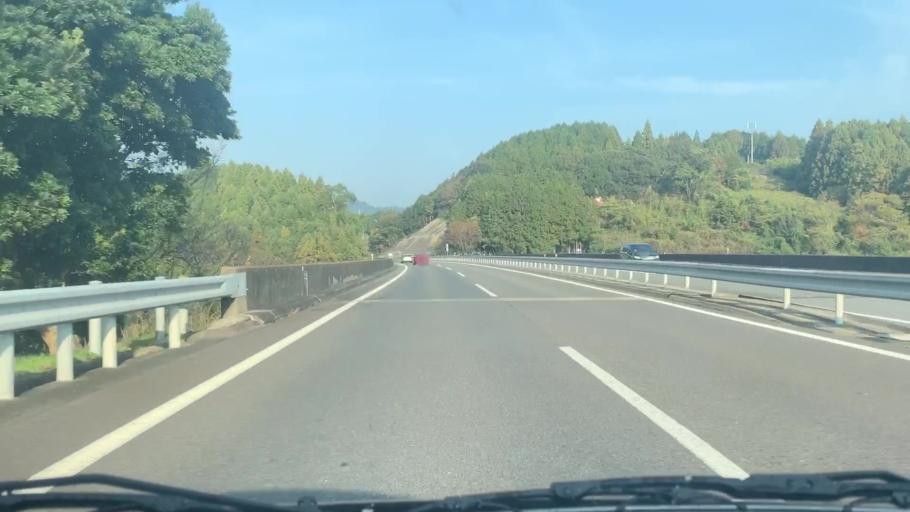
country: JP
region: Saga Prefecture
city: Ureshinomachi-shimojuku
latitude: 33.1518
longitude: 129.9349
